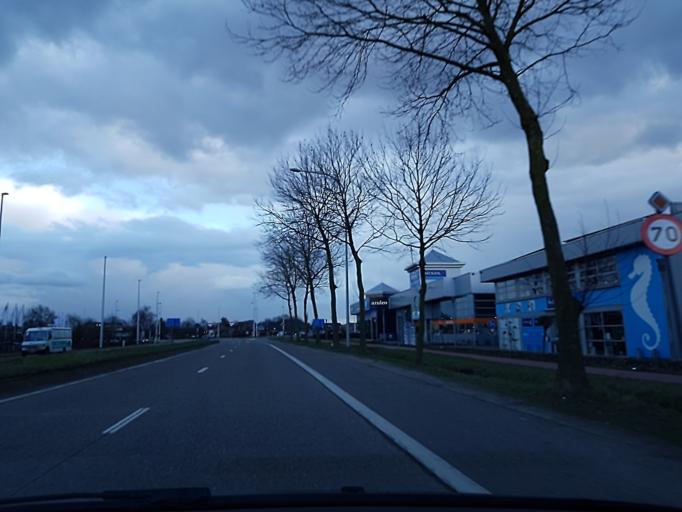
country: BE
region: Flanders
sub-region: Provincie Antwerpen
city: Wijnegem
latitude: 51.2328
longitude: 4.5003
